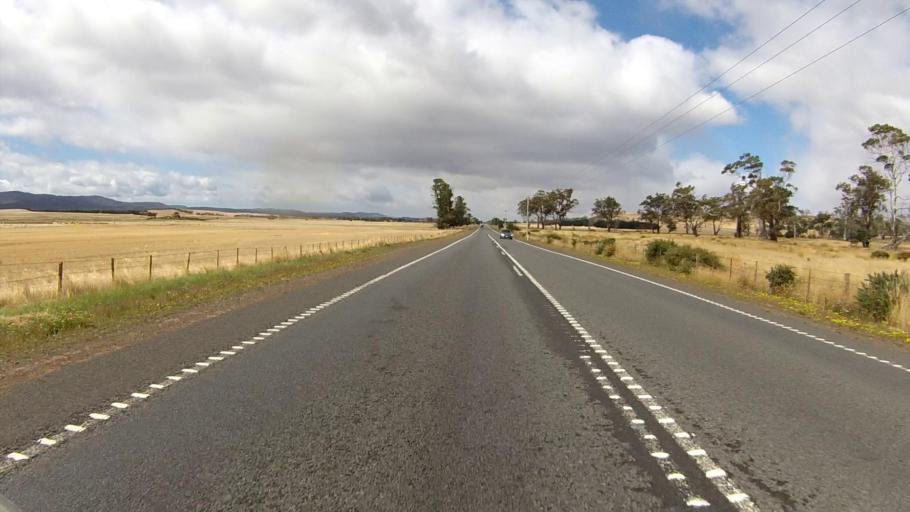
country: AU
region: Tasmania
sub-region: Northern Midlands
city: Evandale
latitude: -41.9548
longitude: 147.4962
